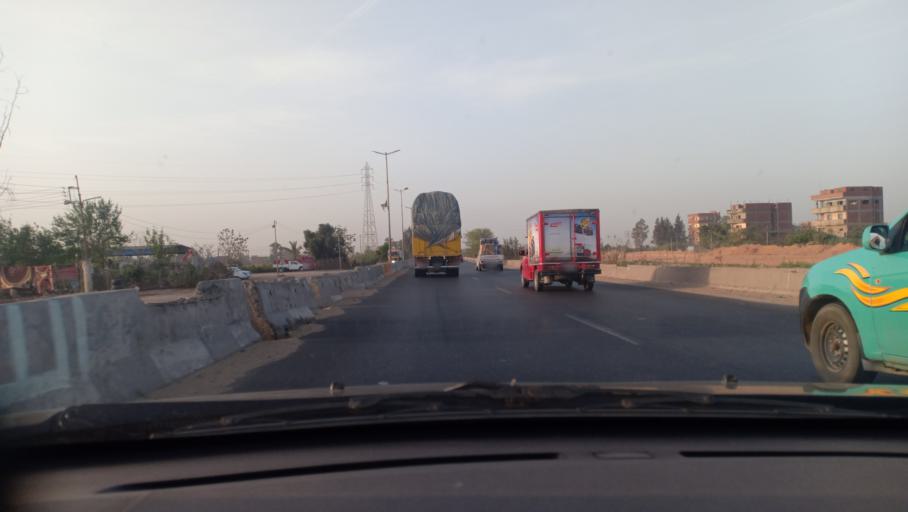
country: EG
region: Muhafazat al Minufiyah
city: Quwaysina
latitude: 30.5644
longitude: 31.2702
